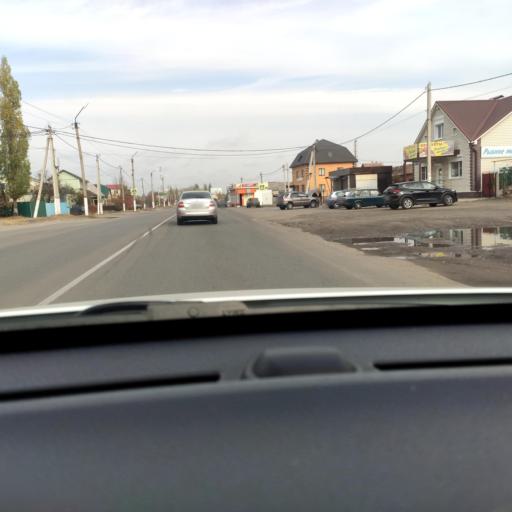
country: RU
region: Voronezj
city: Novaya Usman'
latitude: 51.6290
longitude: 39.4010
